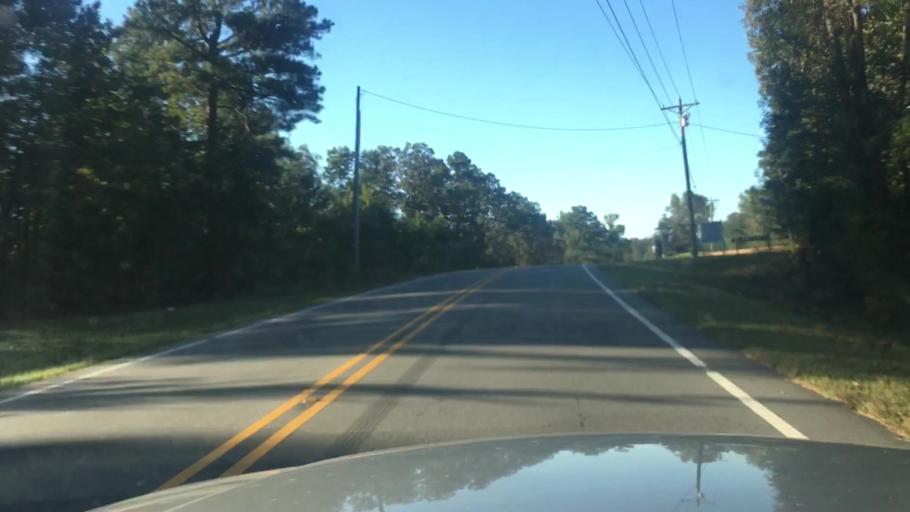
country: US
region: North Carolina
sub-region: Cumberland County
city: Spring Lake
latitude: 35.2614
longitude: -78.9228
